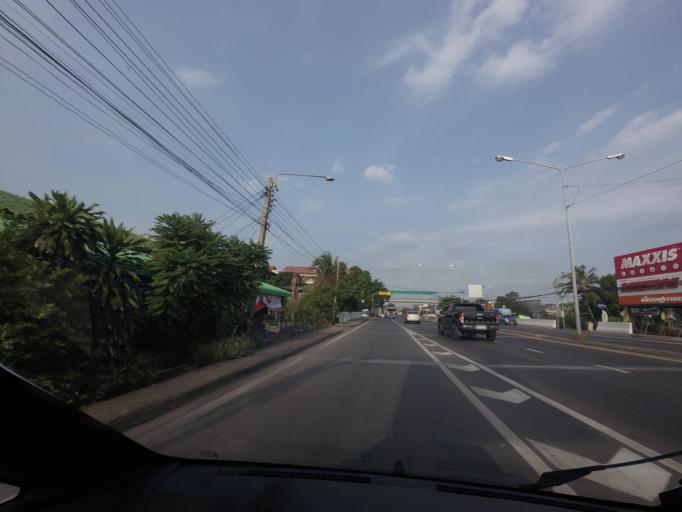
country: TH
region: Bangkok
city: Nong Chok
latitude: 13.8543
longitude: 100.8682
